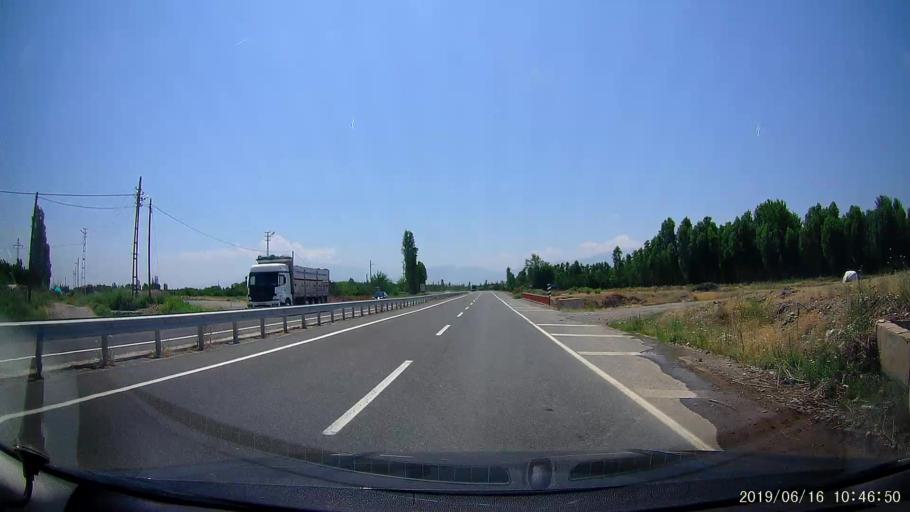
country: AM
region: Armavir
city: Shenavan
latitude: 40.0175
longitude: 43.8820
